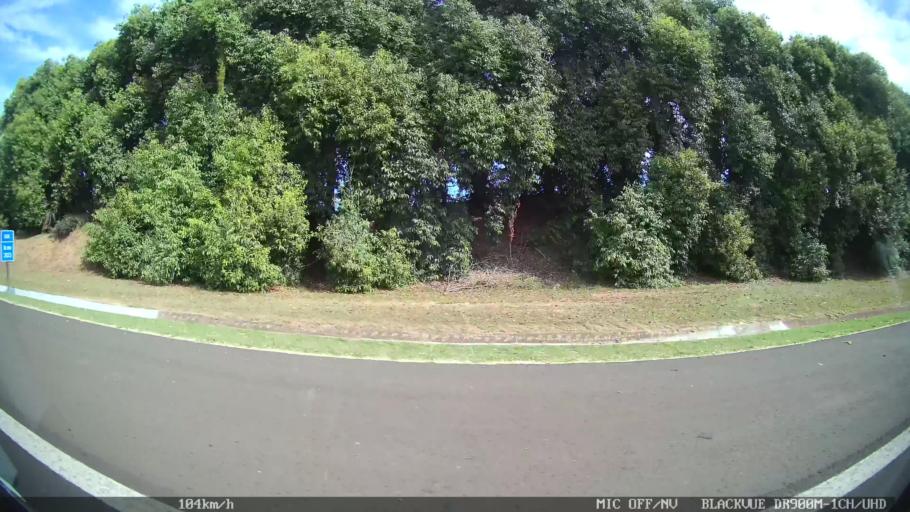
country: BR
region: Sao Paulo
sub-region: Matao
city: Matao
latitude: -21.6303
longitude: -48.4047
